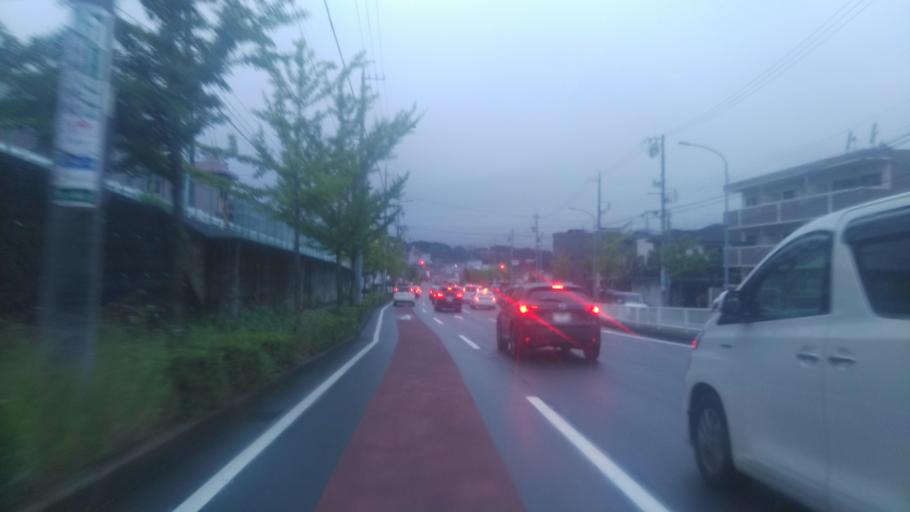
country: JP
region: Aichi
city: Kasugai
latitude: 35.2352
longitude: 137.0012
